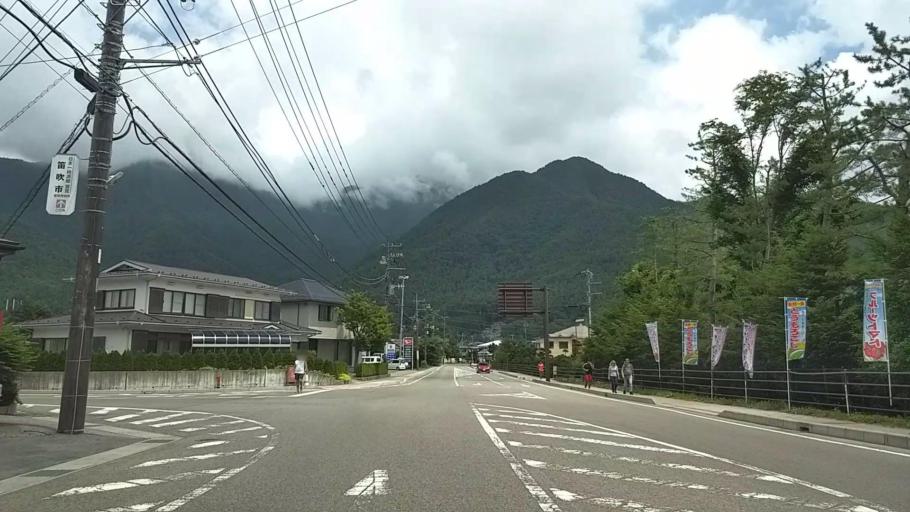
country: JP
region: Yamanashi
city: Fujikawaguchiko
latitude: 35.5205
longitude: 138.7412
